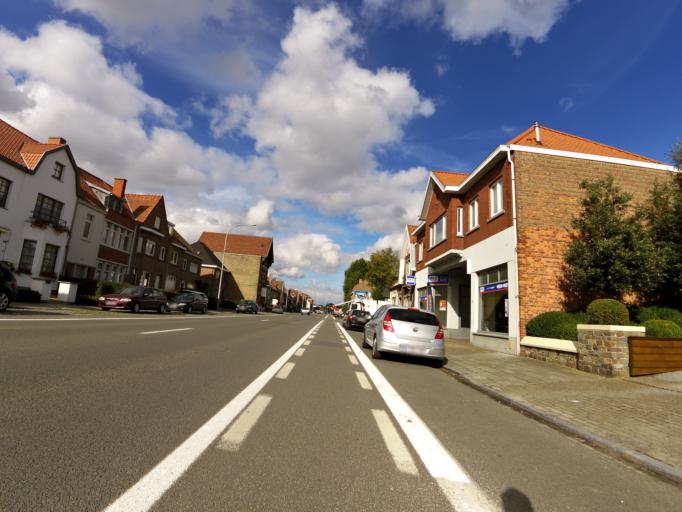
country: BE
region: Flanders
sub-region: Provincie West-Vlaanderen
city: Brugge
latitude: 51.2267
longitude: 3.2280
